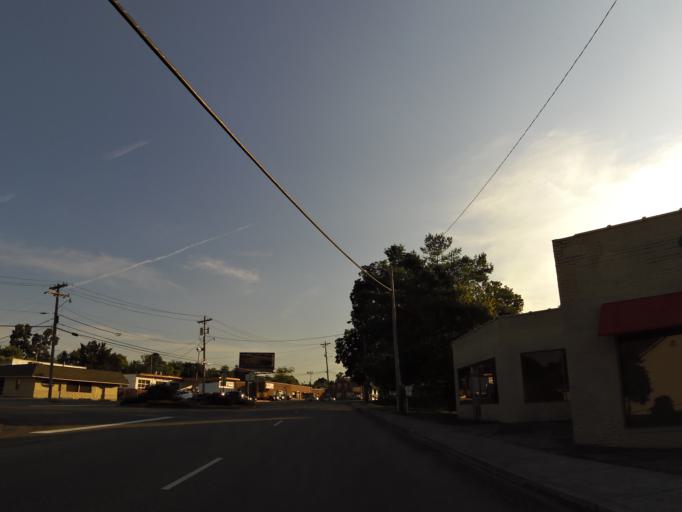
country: US
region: Tennessee
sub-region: McMinn County
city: Athens
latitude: 35.4410
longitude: -84.5984
